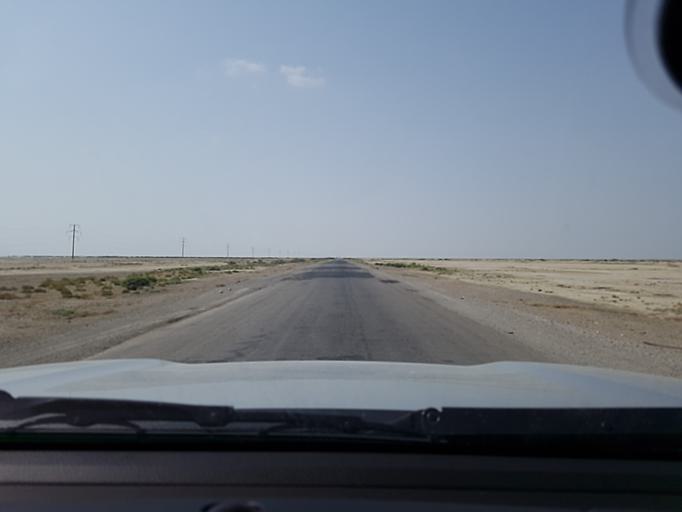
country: TM
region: Balkan
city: Gumdag
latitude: 38.9056
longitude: 54.5920
